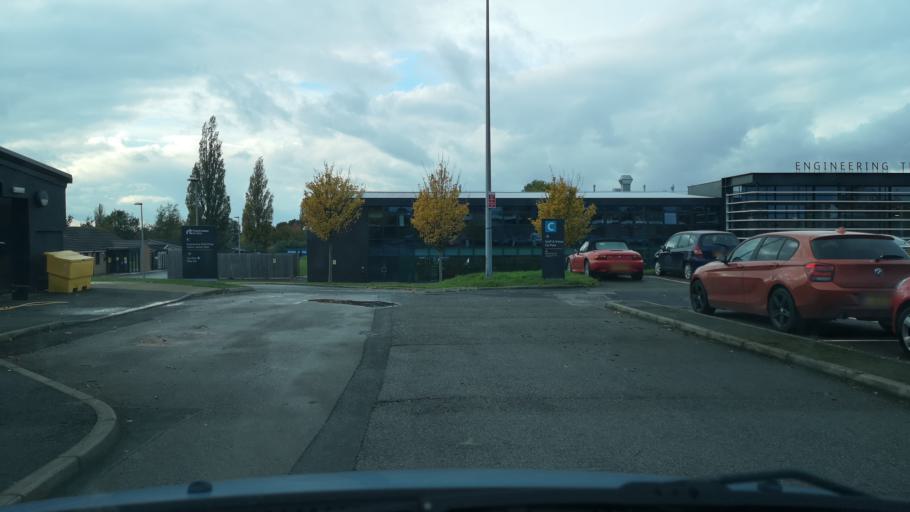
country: GB
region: England
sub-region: North Lincolnshire
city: Scunthorpe
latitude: 53.5771
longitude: -0.6676
